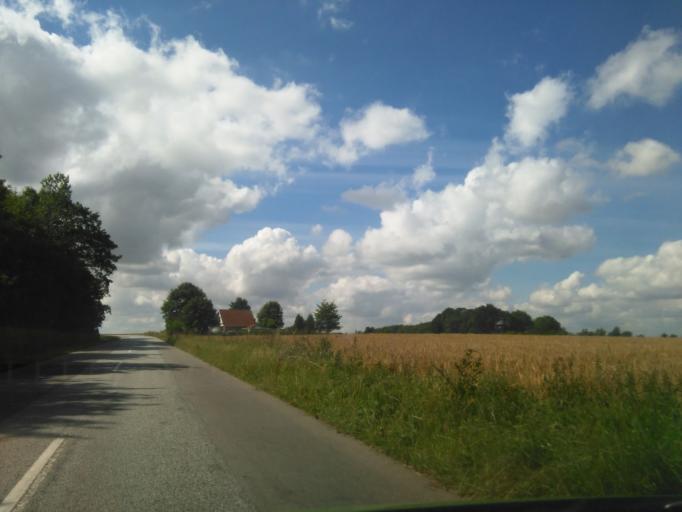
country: DK
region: Central Jutland
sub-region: Arhus Kommune
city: Solbjerg
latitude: 56.0577
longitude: 10.0887
